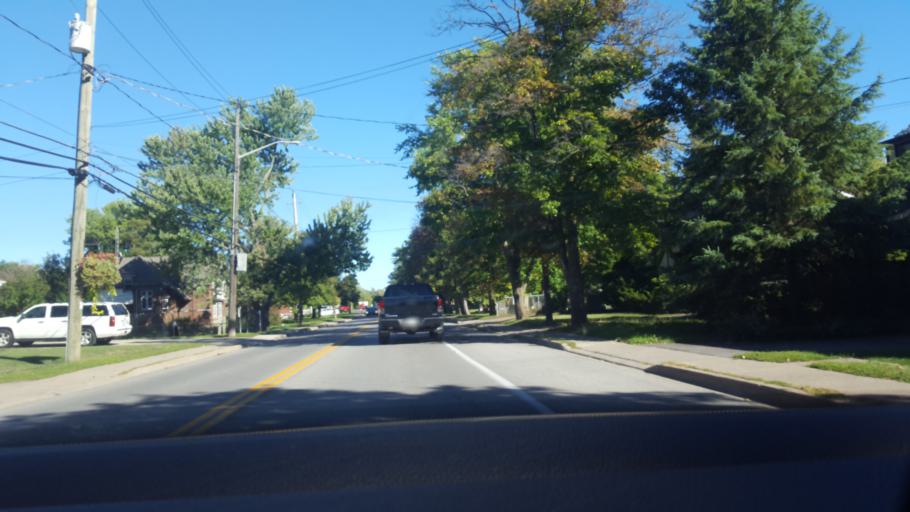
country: CA
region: Ontario
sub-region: Regional Municipality of Niagara
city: St. Catharines
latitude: 43.1005
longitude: -79.5495
